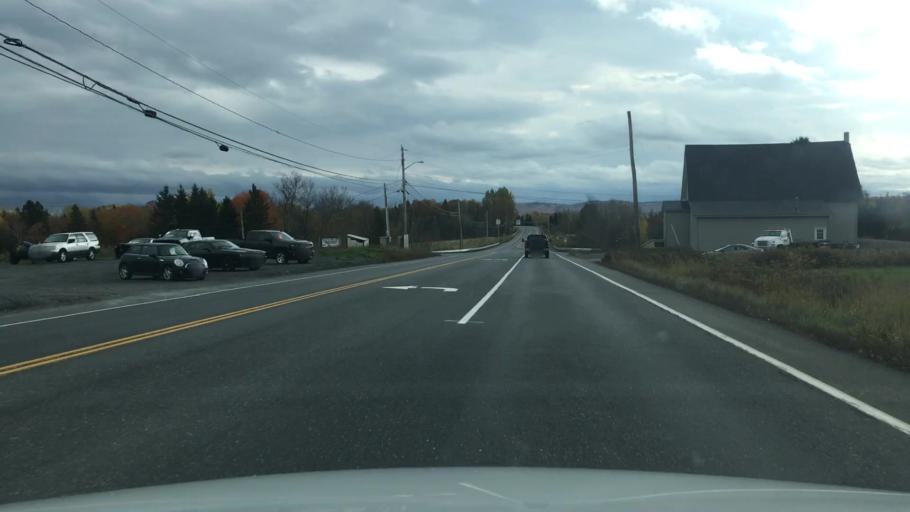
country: US
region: Maine
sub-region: Aroostook County
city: Easton
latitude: 46.5695
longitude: -67.9507
